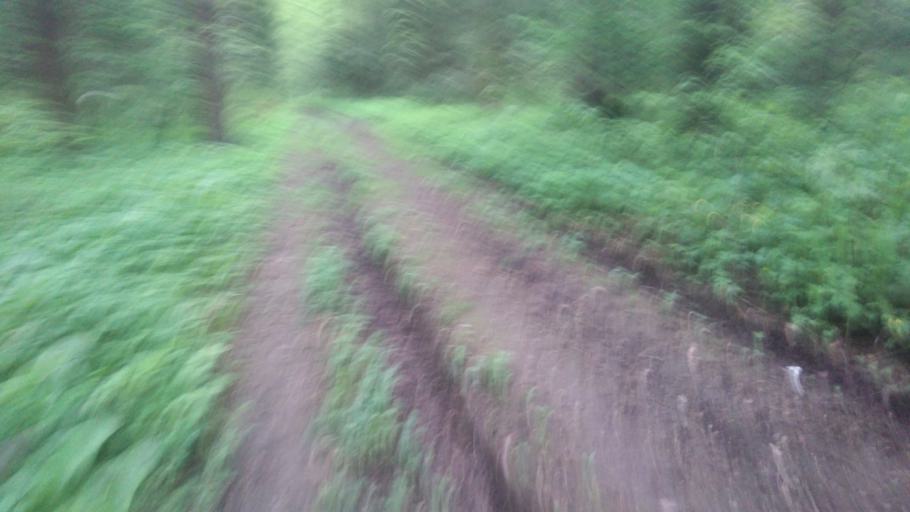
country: RU
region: Perm
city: Froly
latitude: 57.9623
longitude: 56.2987
